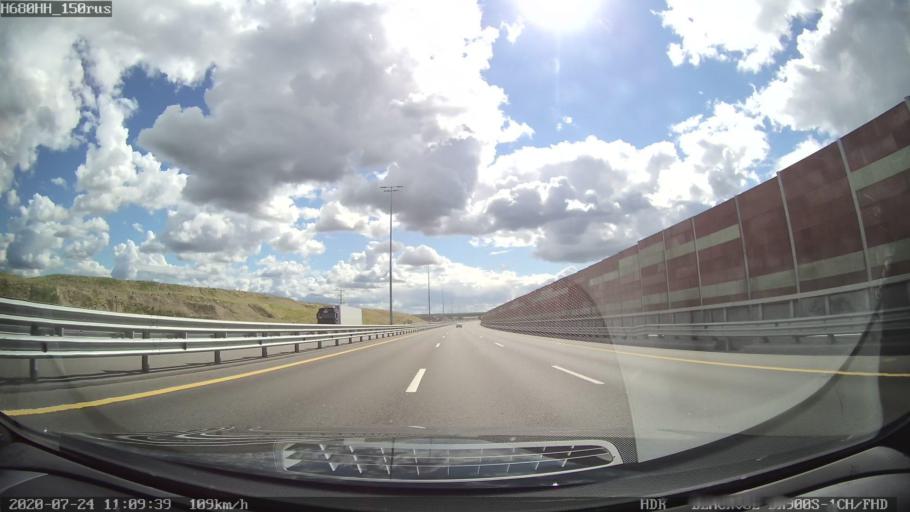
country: RU
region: St.-Petersburg
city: Tyarlevo
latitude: 59.7478
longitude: 30.4804
